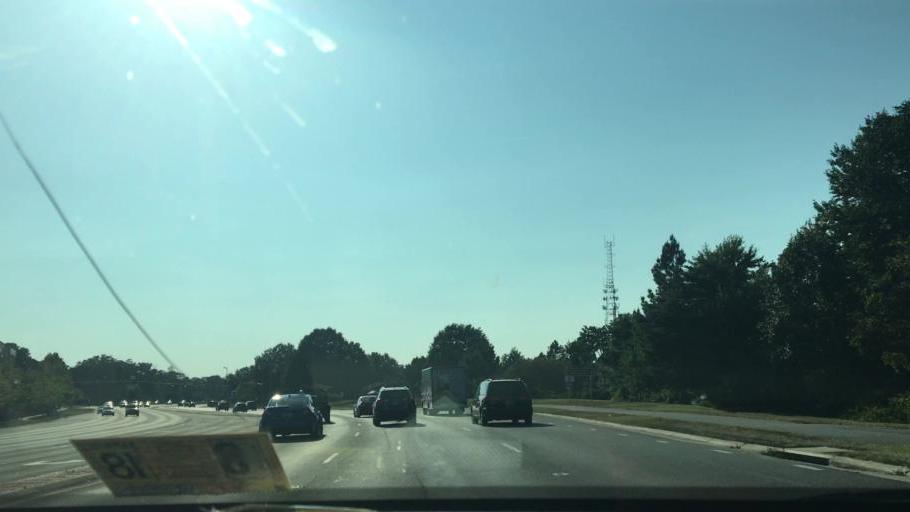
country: US
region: Virginia
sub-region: Prince William County
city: Lake Ridge
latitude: 38.6785
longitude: -77.3493
